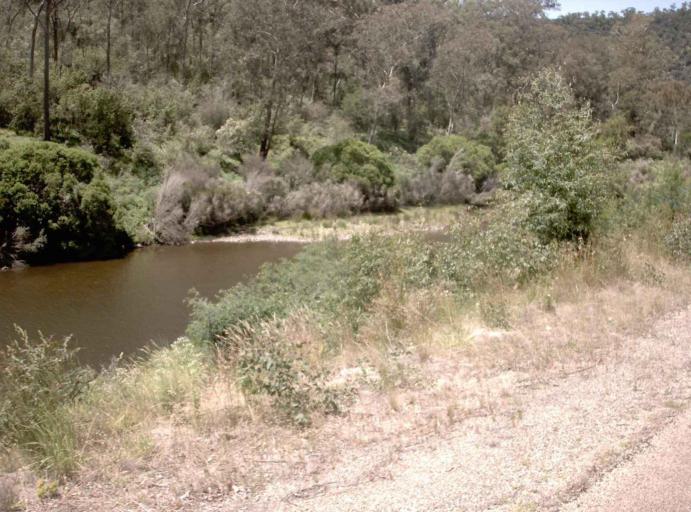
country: AU
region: Victoria
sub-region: East Gippsland
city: Lakes Entrance
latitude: -37.5457
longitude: 147.8661
